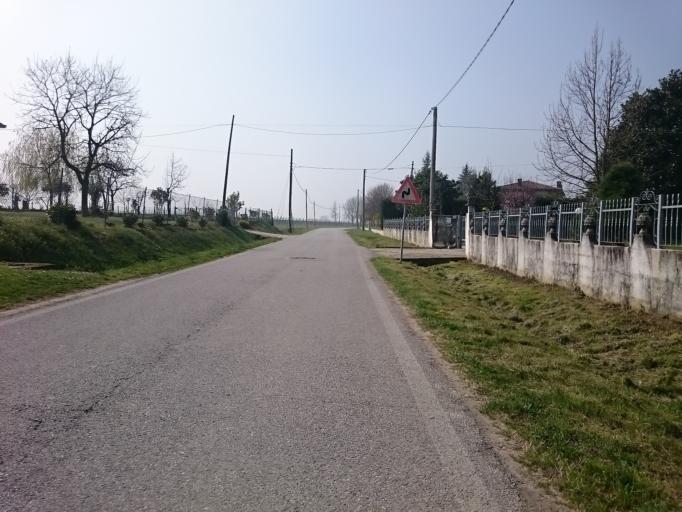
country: IT
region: Veneto
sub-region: Provincia di Padova
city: Pernumia
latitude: 45.2679
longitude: 11.8049
